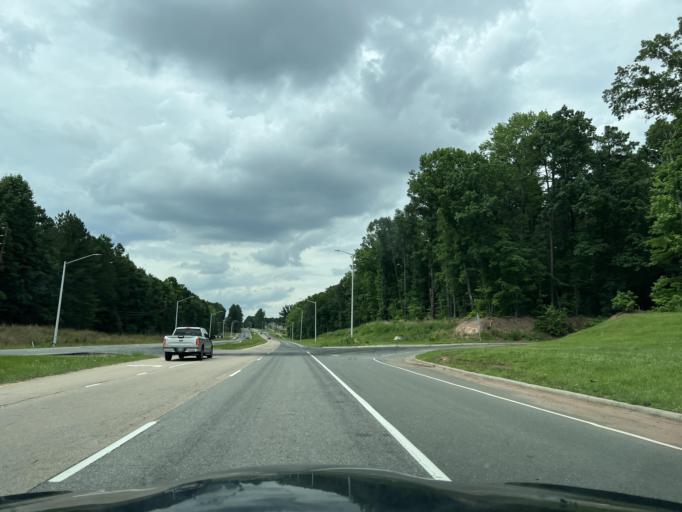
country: US
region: North Carolina
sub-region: Durham County
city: Durham
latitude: 35.9461
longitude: -78.8879
